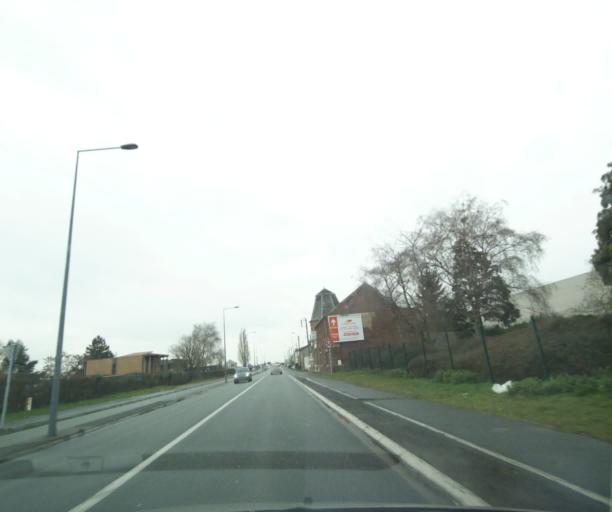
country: FR
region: Nord-Pas-de-Calais
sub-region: Departement du Nord
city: Prouvy
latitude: 50.3325
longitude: 3.4528
